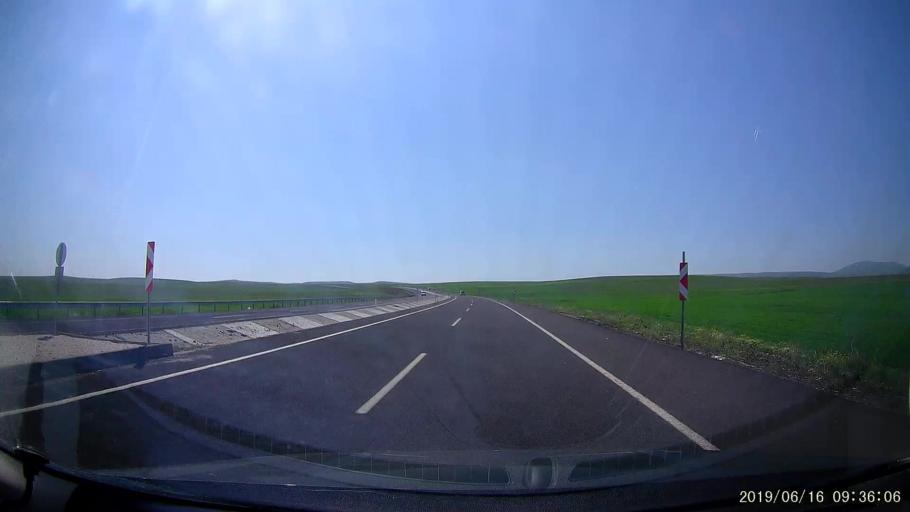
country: TR
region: Kars
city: Kars
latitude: 40.5617
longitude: 43.1666
